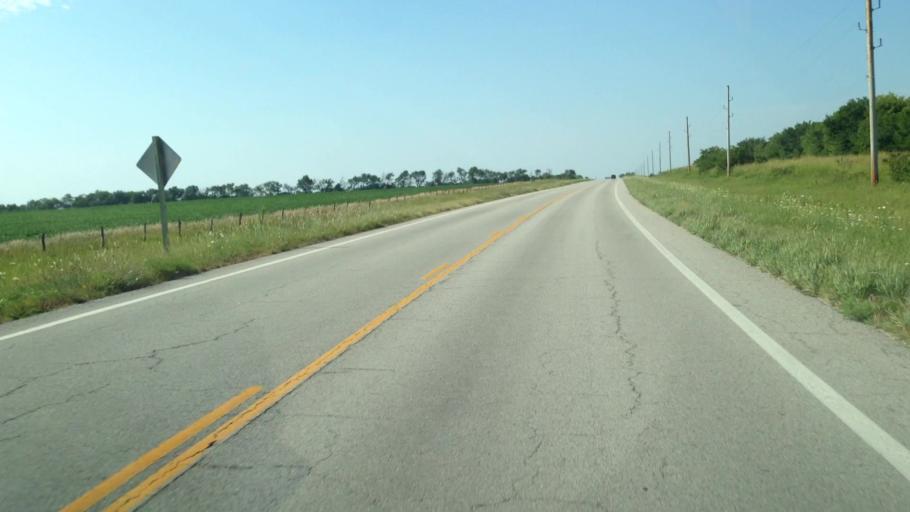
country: US
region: Kansas
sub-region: Allen County
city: Iola
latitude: 38.0104
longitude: -95.1709
